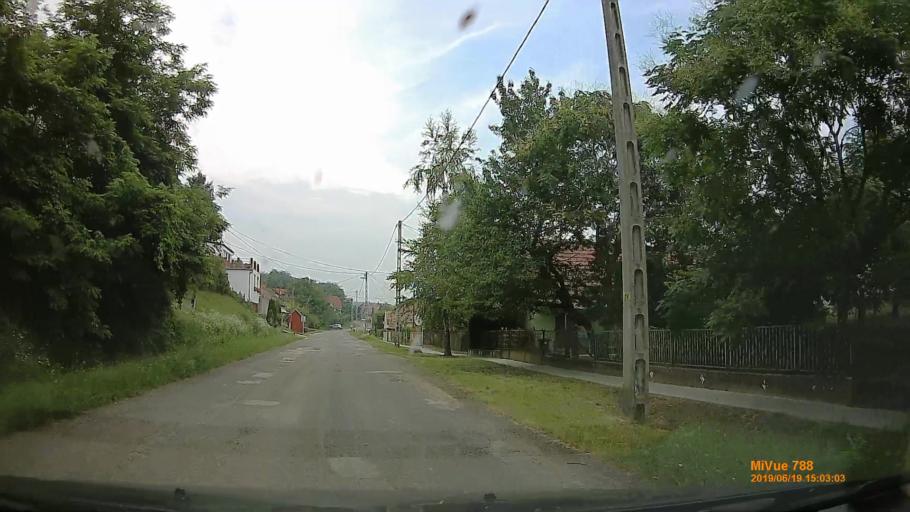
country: HU
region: Baranya
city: Szigetvar
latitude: 46.0923
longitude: 17.8051
